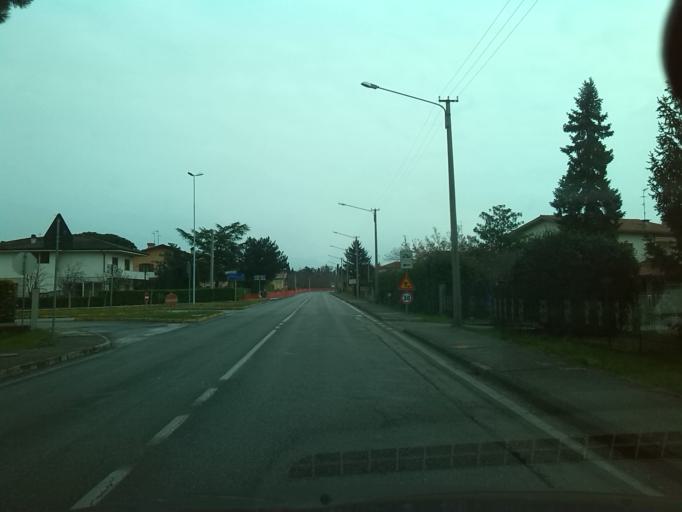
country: IT
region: Friuli Venezia Giulia
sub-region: Provincia di Gorizia
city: Capriva del Friuli
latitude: 45.9392
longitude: 13.5082
